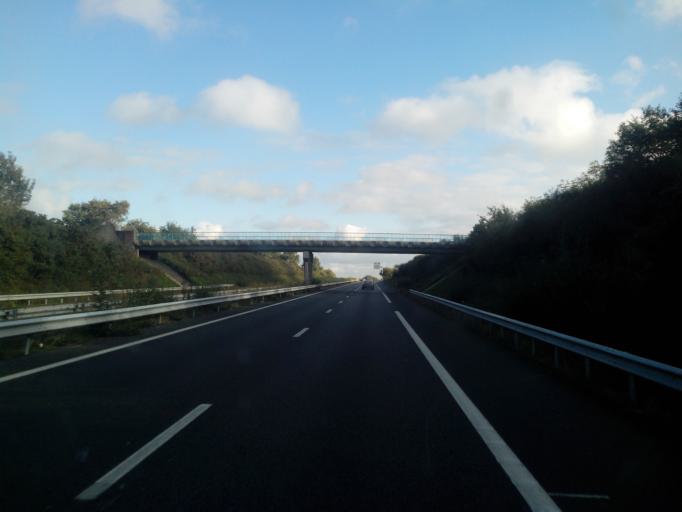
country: FR
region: Brittany
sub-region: Departement du Morbihan
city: Nivillac
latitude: 47.5079
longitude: -2.2714
